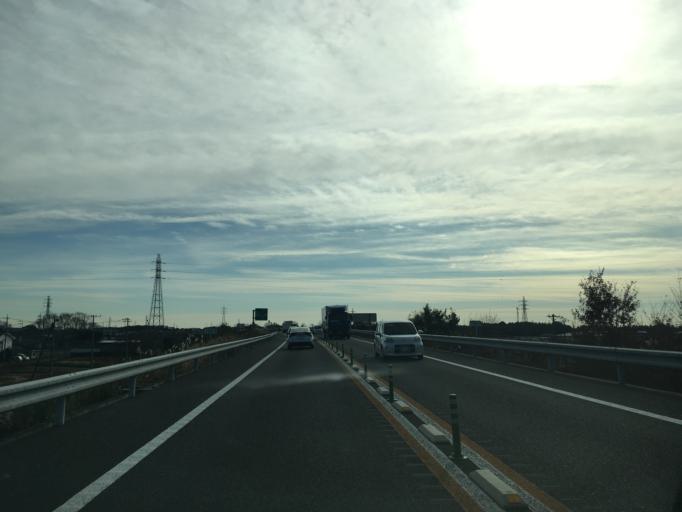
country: JP
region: Ibaraki
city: Naka
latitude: 36.0475
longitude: 140.1065
